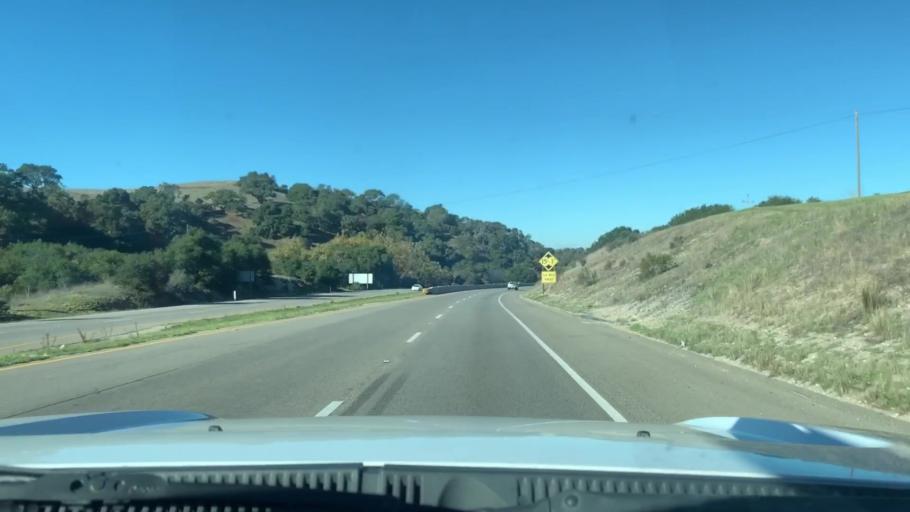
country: US
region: California
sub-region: San Luis Obispo County
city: Arroyo Grande
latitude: 35.1117
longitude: -120.5648
